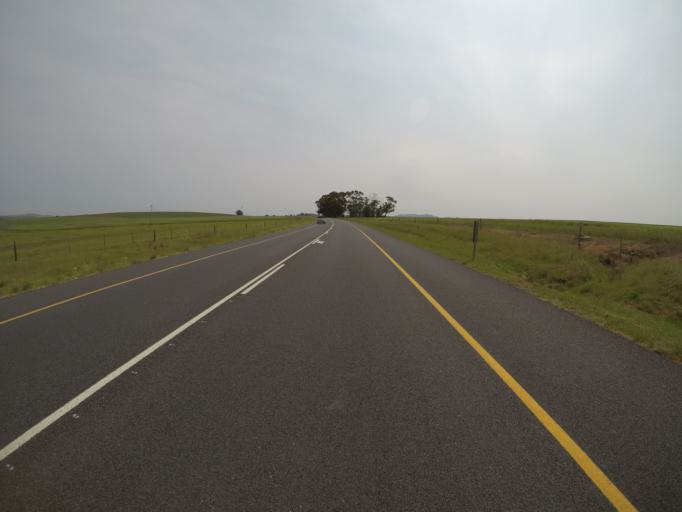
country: ZA
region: Western Cape
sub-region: West Coast District Municipality
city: Malmesbury
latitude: -33.5135
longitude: 18.8456
